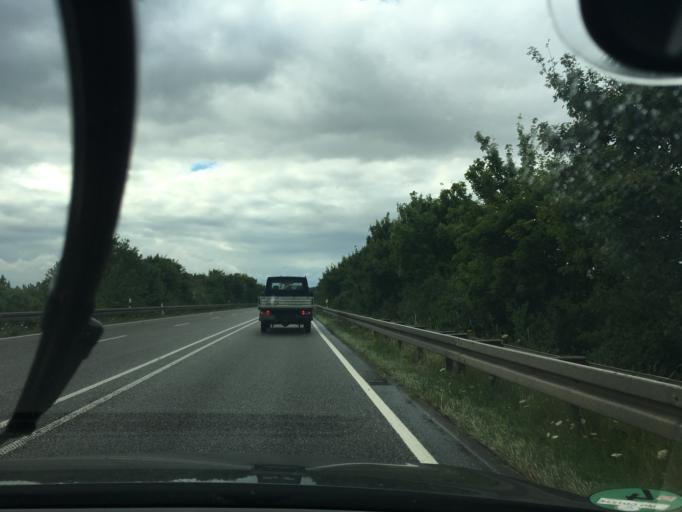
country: DE
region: North Rhine-Westphalia
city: Zulpich
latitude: 50.6833
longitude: 6.7122
